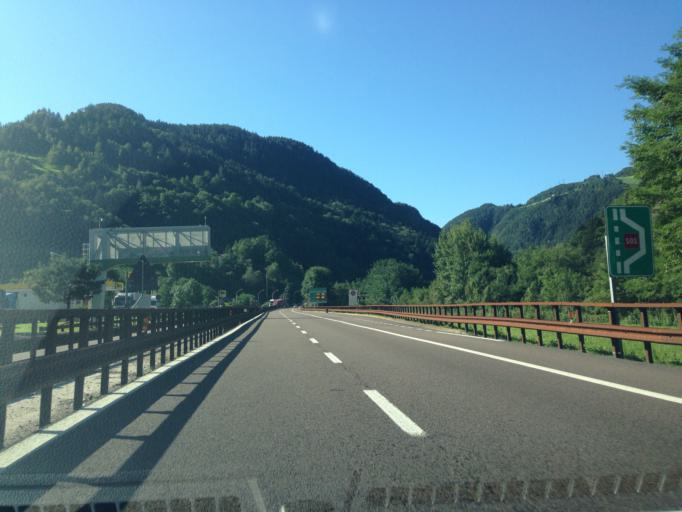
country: IT
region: Trentino-Alto Adige
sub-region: Bolzano
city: Ponte Gardena
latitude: 46.5714
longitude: 11.5229
